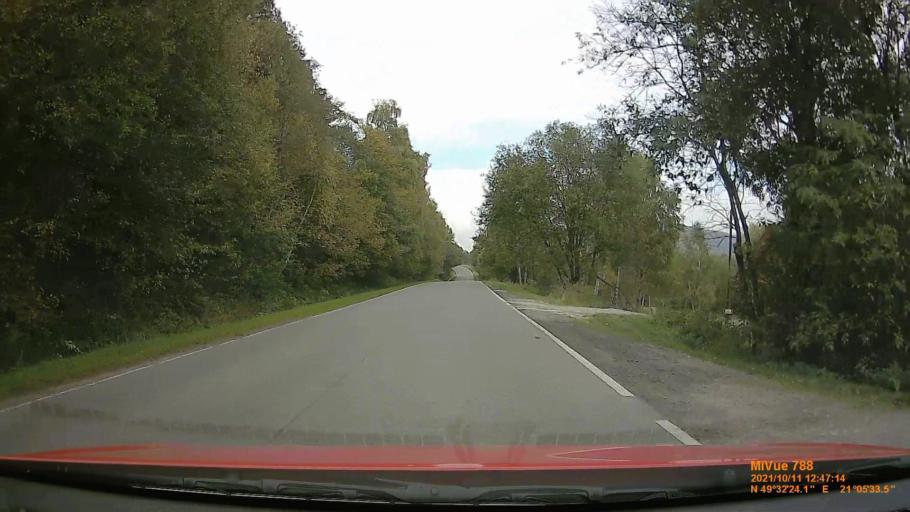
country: PL
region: Lesser Poland Voivodeship
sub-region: Powiat gorlicki
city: Uscie Gorlickie
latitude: 49.5402
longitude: 21.0925
